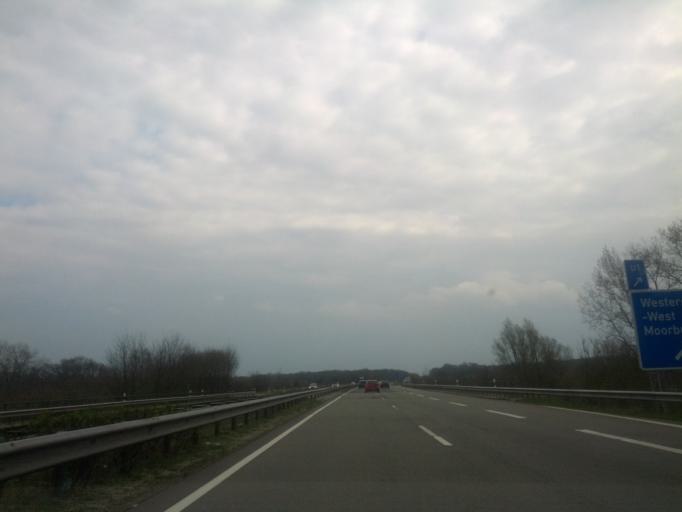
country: DE
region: Lower Saxony
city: Westerstede
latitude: 53.2809
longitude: 7.9001
